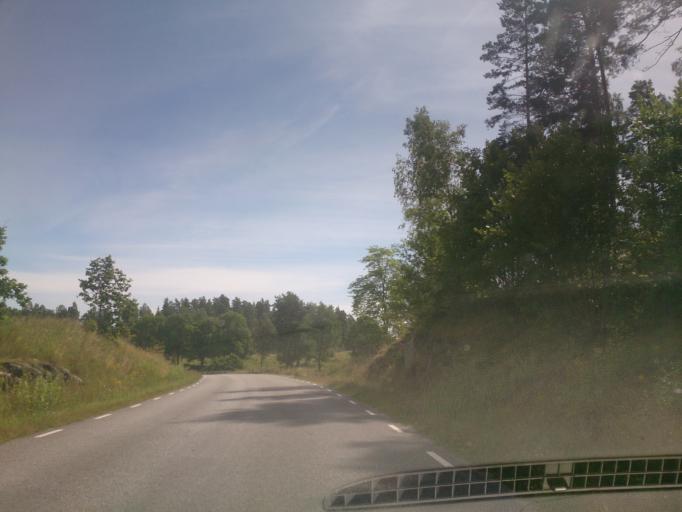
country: SE
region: OEstergoetland
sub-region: Valdemarsviks Kommun
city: Valdemarsvik
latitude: 58.3378
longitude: 16.6189
